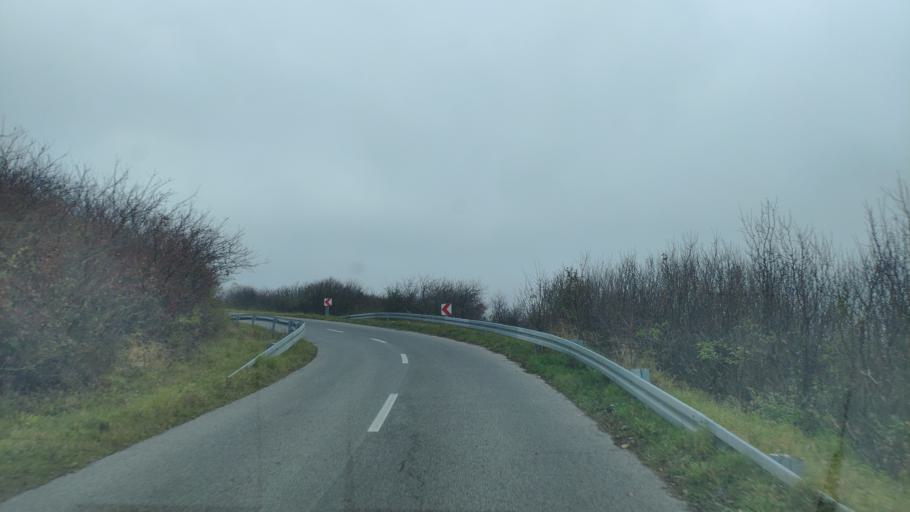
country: SK
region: Presovsky
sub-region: Okres Presov
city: Presov
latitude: 49.1285
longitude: 21.2561
